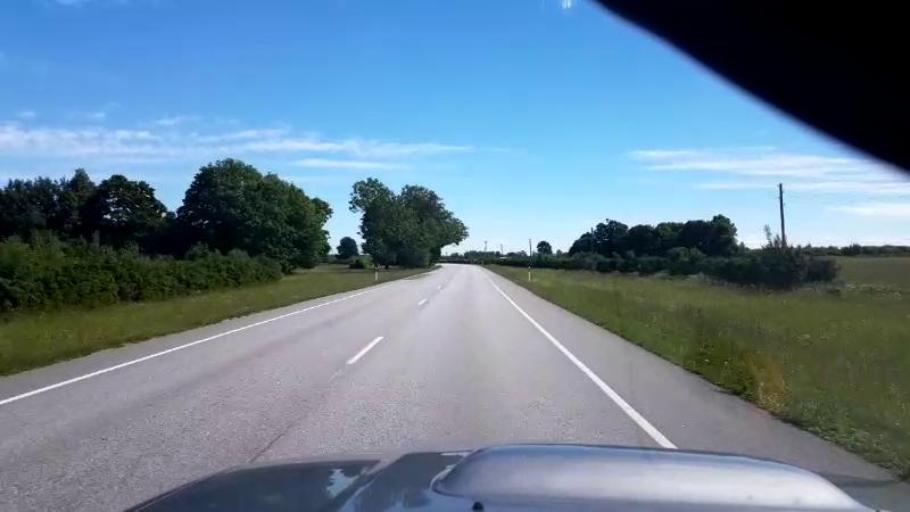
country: EE
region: Jaervamaa
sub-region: Koeru vald
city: Koeru
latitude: 58.9900
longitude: 25.9707
